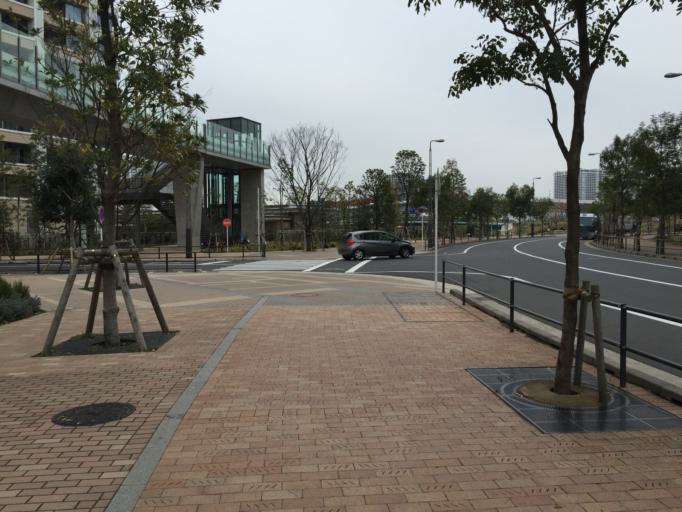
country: JP
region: Tokyo
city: Urayasu
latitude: 35.6481
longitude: 139.7920
